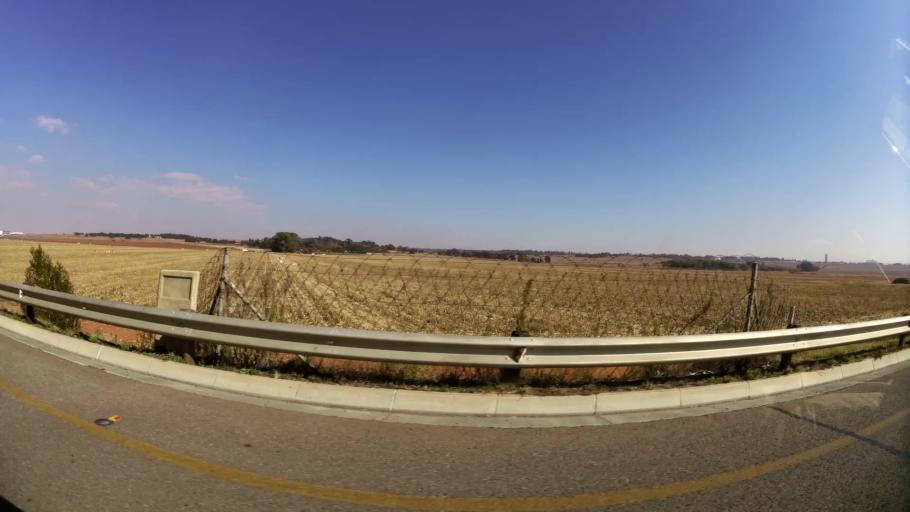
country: ZA
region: Gauteng
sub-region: Ekurhuleni Metropolitan Municipality
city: Tembisa
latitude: -26.0532
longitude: 28.2810
